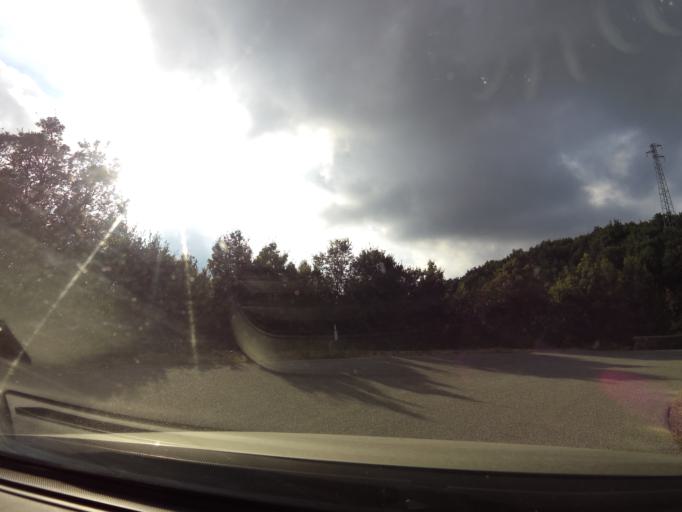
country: IT
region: Calabria
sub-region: Provincia di Vibo-Valentia
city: Nardodipace
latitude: 38.4766
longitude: 16.3860
